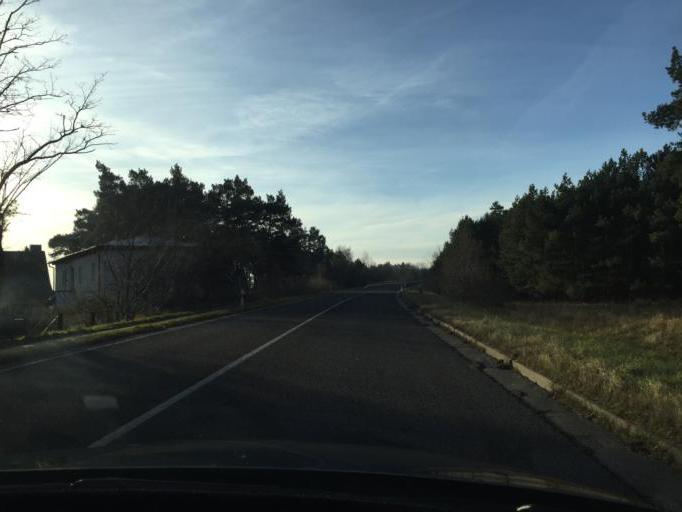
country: DE
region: Brandenburg
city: Ziltendorf
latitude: 52.2051
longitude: 14.6177
